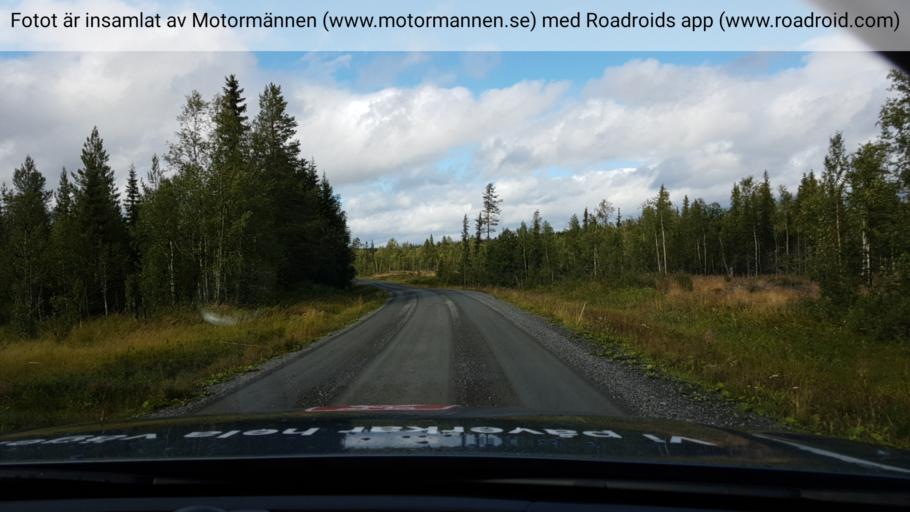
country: SE
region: Jaemtland
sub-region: Krokoms Kommun
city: Krokom
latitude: 63.7219
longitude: 14.5154
